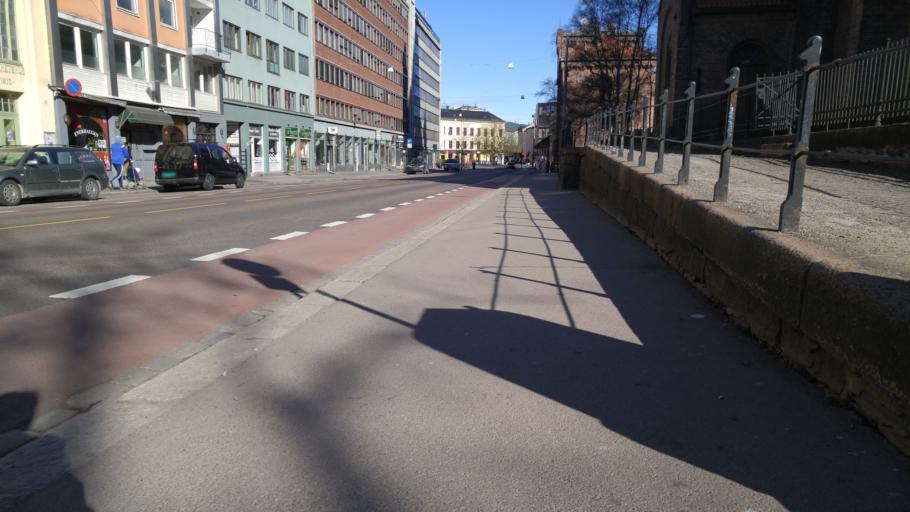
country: NO
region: Oslo
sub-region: Oslo
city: Oslo
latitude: 59.9108
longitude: 10.7675
